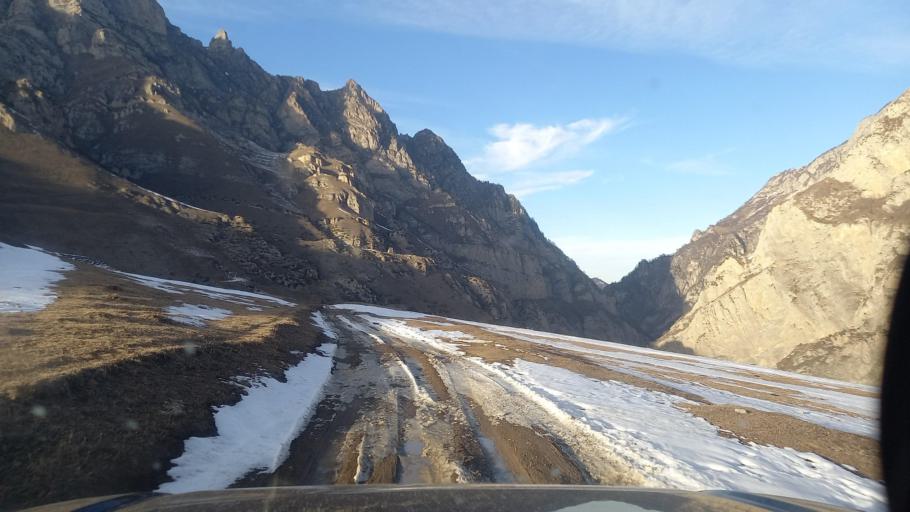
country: RU
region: Ingushetiya
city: Dzhayrakh
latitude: 42.8551
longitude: 44.5158
